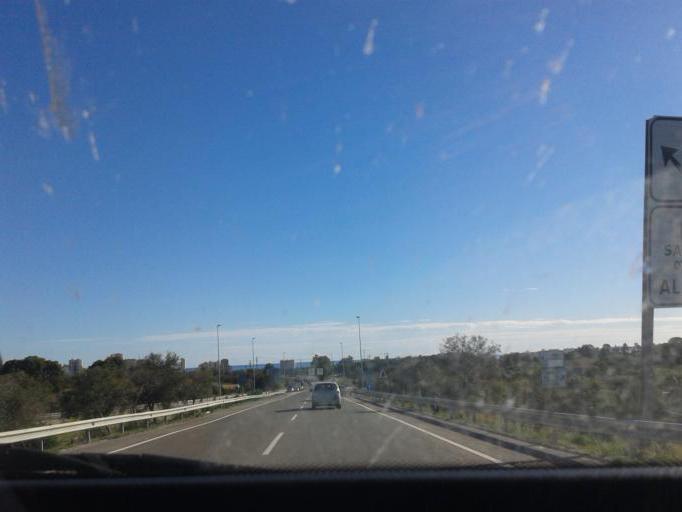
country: ES
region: Valencia
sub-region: Provincia de Alicante
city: Muchamiel
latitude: 38.4188
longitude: -0.4253
